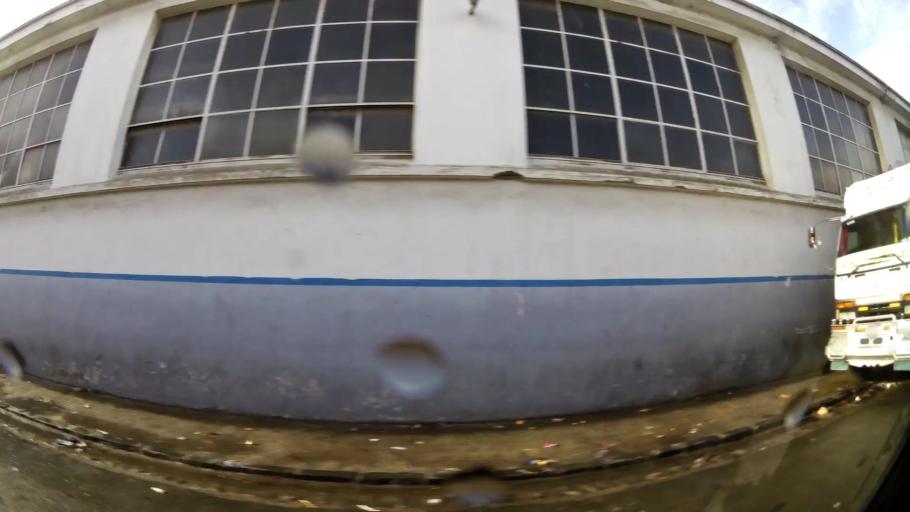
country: MA
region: Grand Casablanca
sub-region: Casablanca
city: Casablanca
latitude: 33.5887
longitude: -7.5986
